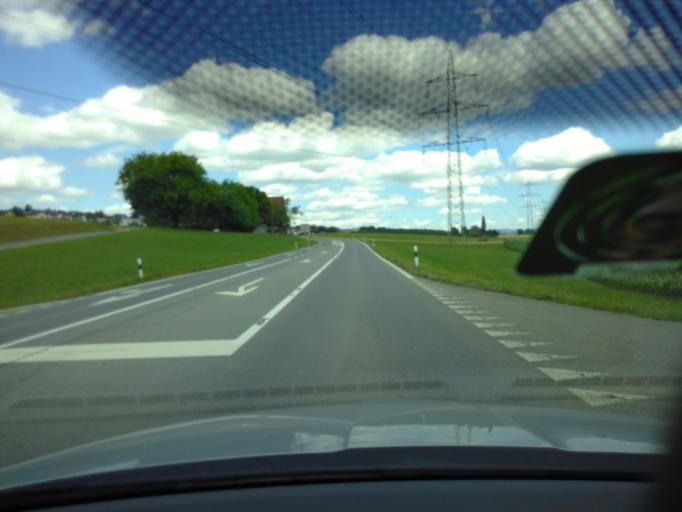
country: CH
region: Aargau
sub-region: Bezirk Muri
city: Oberruti
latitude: 47.1410
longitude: 8.3958
